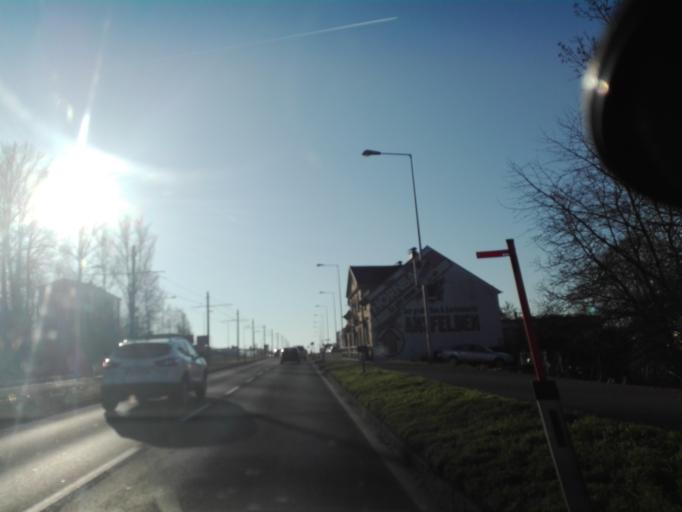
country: AT
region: Upper Austria
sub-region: Politischer Bezirk Linz-Land
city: Leonding
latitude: 48.2739
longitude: 14.2720
